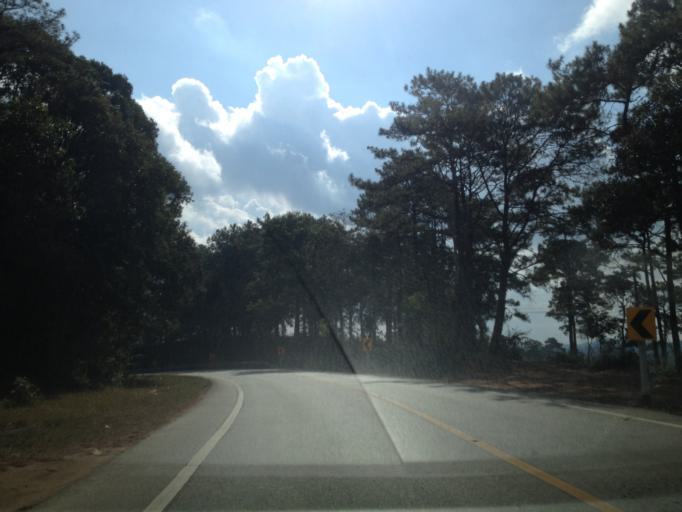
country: TH
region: Chiang Mai
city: Hot
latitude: 18.1389
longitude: 98.3302
